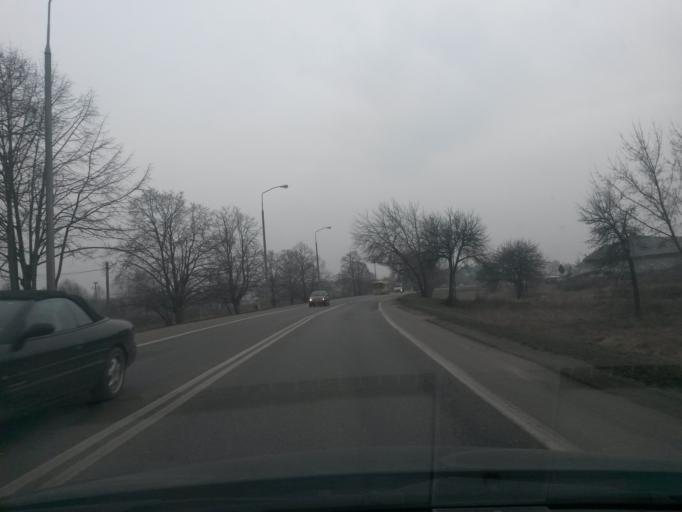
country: PL
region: Masovian Voivodeship
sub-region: Powiat legionowski
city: Nieporet
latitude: 52.4335
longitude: 21.0265
